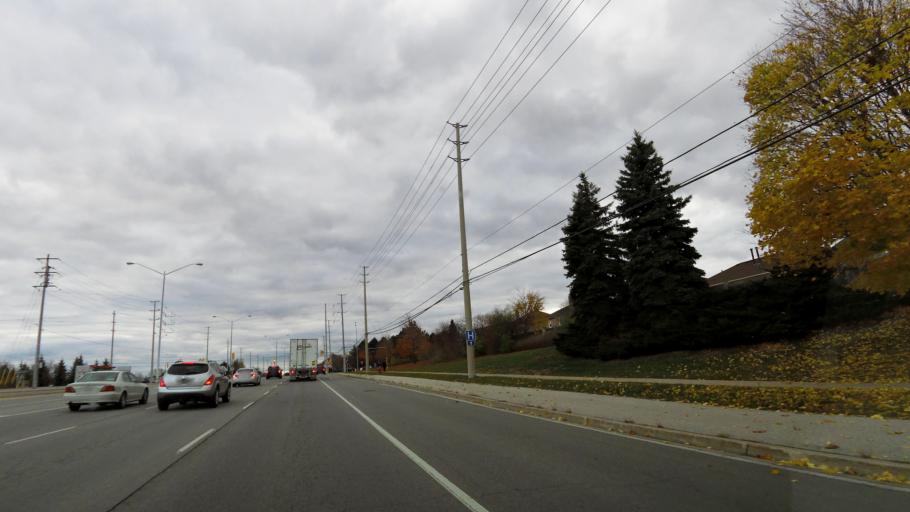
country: CA
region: Ontario
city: Brampton
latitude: 43.7556
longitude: -79.7328
